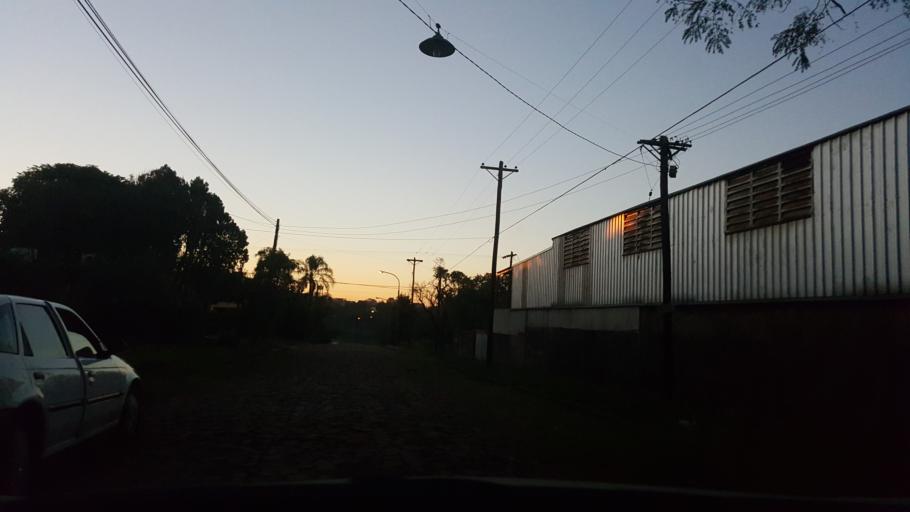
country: AR
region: Misiones
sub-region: Departamento de Capital
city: Posadas
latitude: -27.4227
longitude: -55.9003
